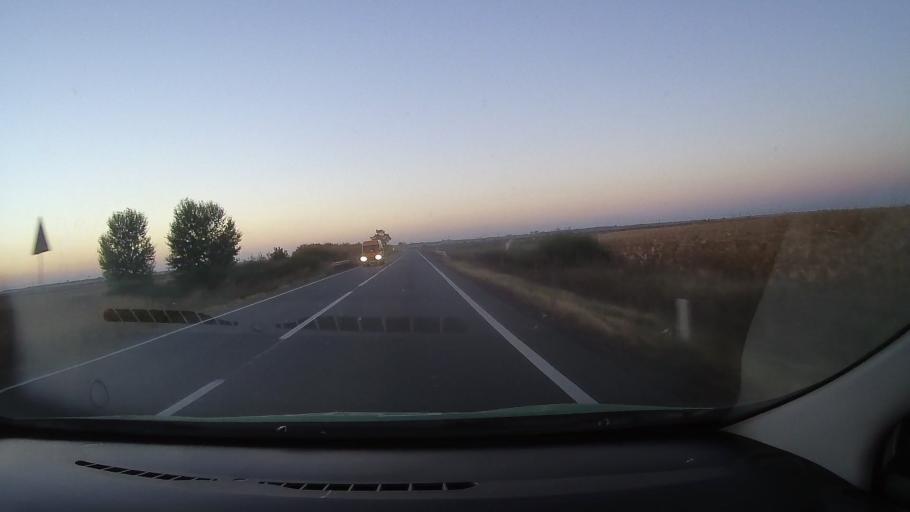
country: RO
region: Bihor
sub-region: Comuna Tarcea
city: Tarcea
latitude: 47.4409
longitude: 22.1922
